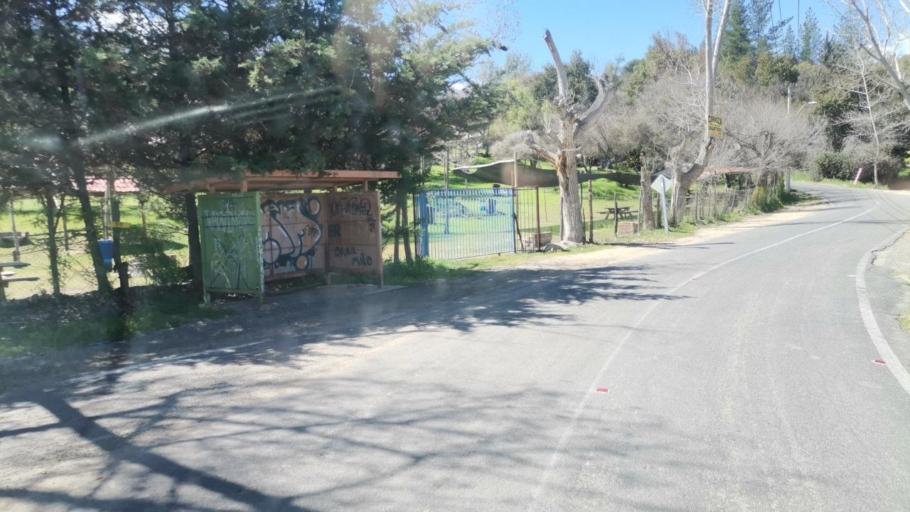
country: CL
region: Valparaiso
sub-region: Provincia de Marga Marga
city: Limache
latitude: -33.1744
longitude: -71.1680
